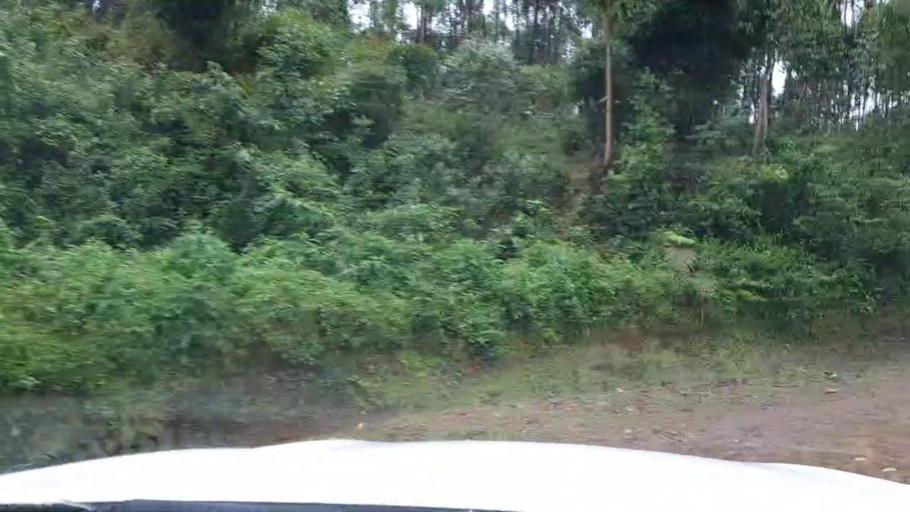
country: RW
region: Western Province
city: Cyangugu
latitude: -2.4633
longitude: 29.0334
